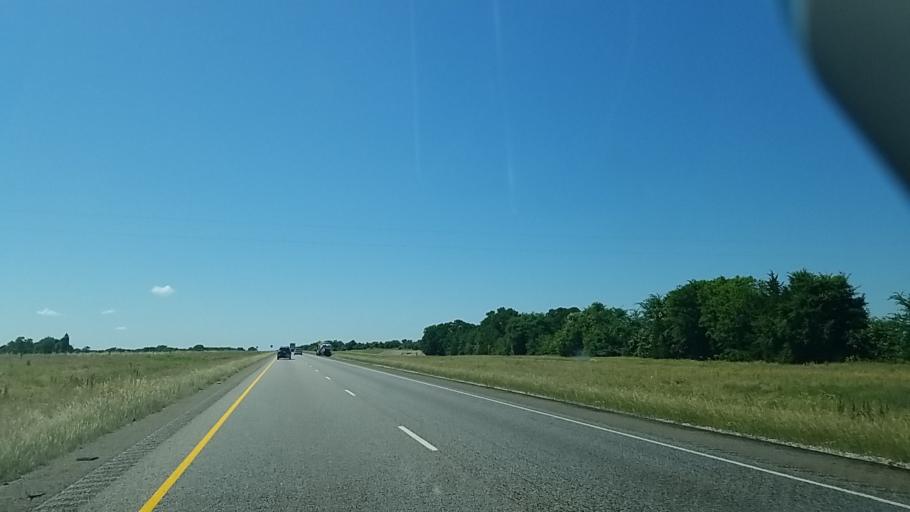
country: US
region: Texas
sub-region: Freestone County
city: Fairfield
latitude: 31.7685
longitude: -96.2180
